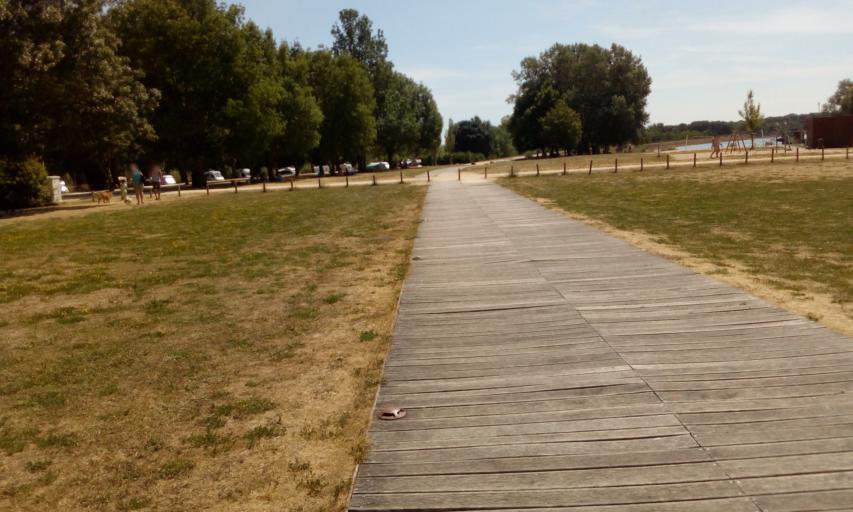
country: FR
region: Lorraine
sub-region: Departement de la Meuse
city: Vigneulles-les-Hattonchatel
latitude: 48.9267
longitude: 5.7563
